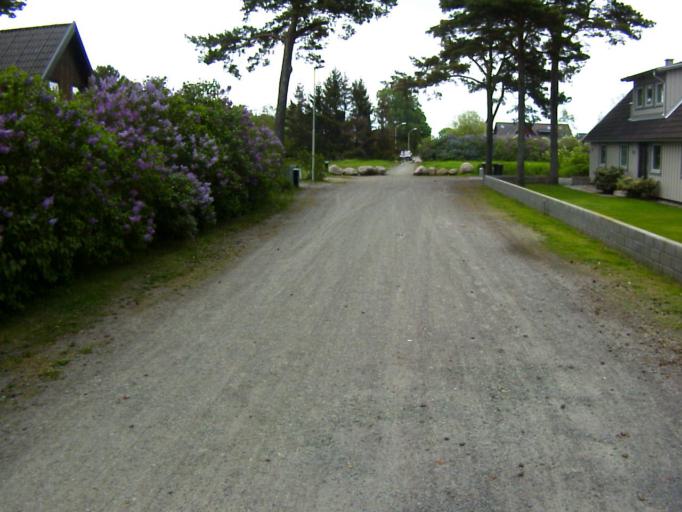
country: SE
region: Skane
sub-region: Kristianstads Kommun
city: Ahus
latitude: 55.9204
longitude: 14.2766
